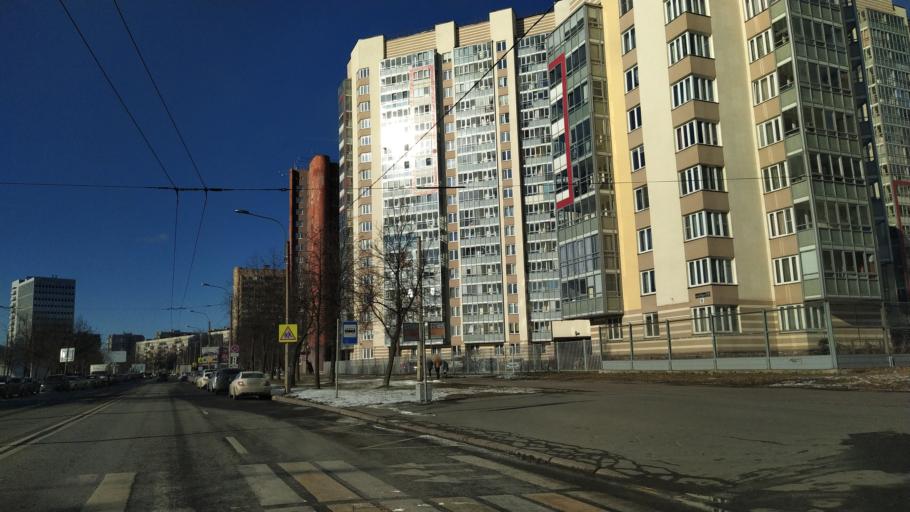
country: RU
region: Leningrad
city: Kalininskiy
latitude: 59.9686
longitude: 30.4267
